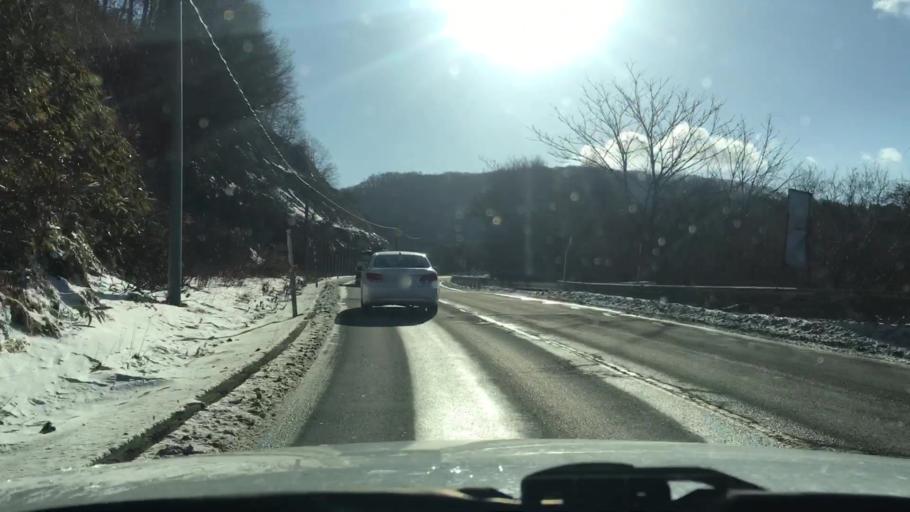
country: JP
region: Iwate
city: Morioka-shi
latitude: 39.6590
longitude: 141.3377
